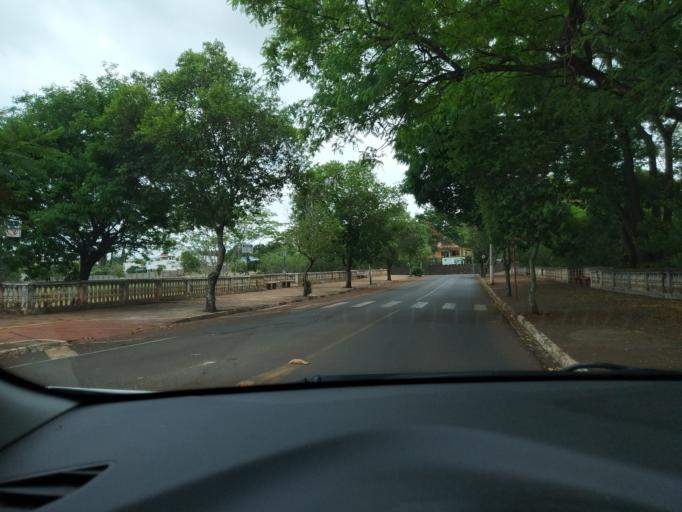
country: BR
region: Sao Paulo
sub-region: Jau
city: Jau
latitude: -22.2760
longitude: -48.5480
